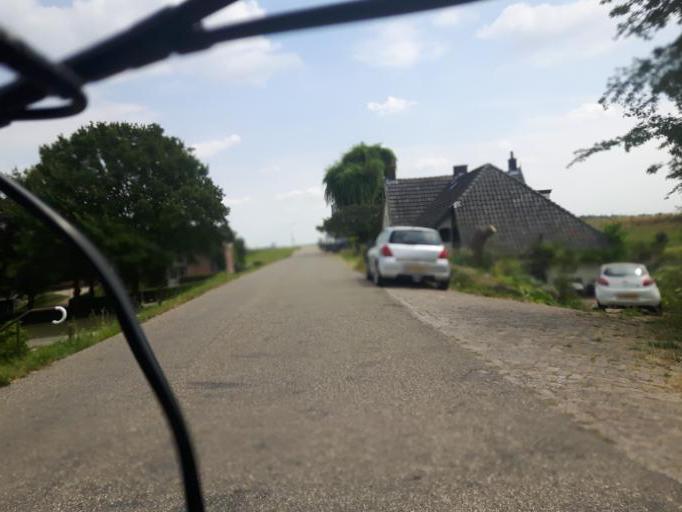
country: NL
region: Gelderland
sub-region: Gemeente Zaltbommel
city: Nederhemert
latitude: 51.8187
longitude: 5.1553
